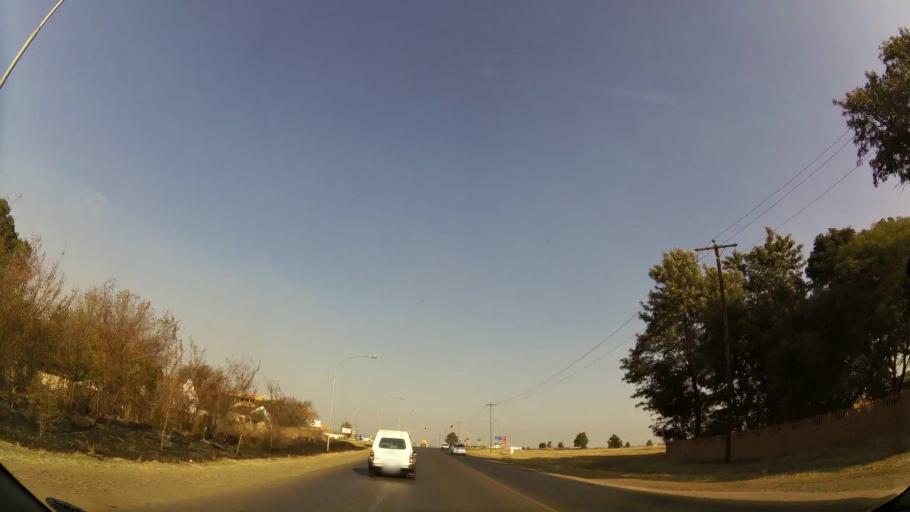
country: ZA
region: Gauteng
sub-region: Ekurhuleni Metropolitan Municipality
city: Benoni
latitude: -26.1377
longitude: 28.3910
